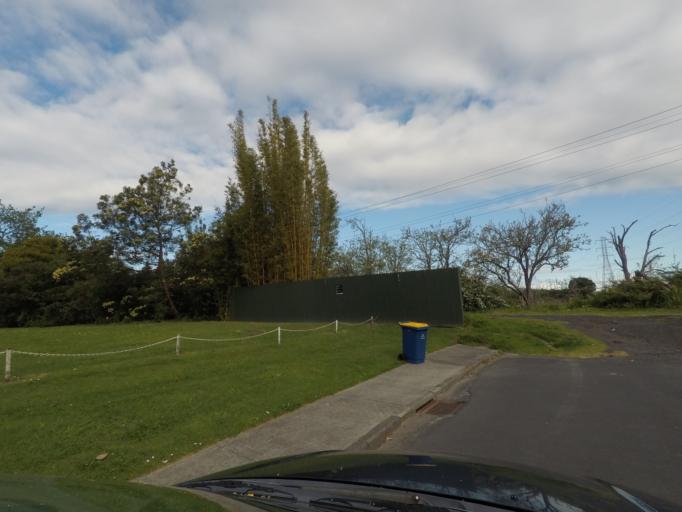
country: NZ
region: Auckland
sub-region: Auckland
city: Rosebank
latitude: -36.8821
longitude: 174.6591
